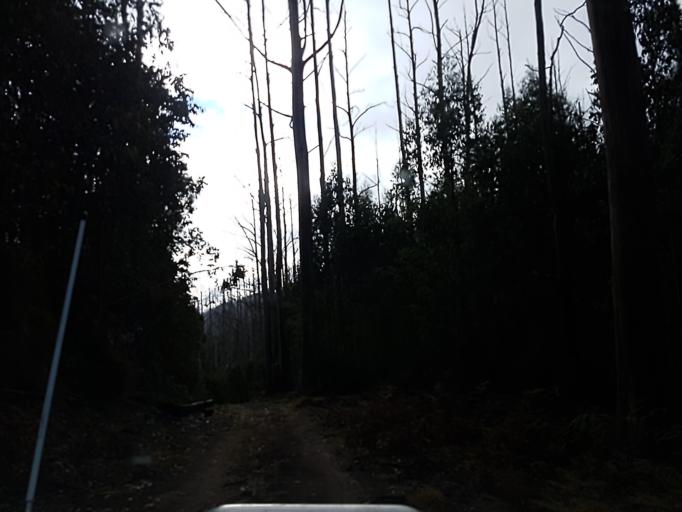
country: AU
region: Victoria
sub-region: Yarra Ranges
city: Millgrove
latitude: -37.5665
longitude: 145.7570
